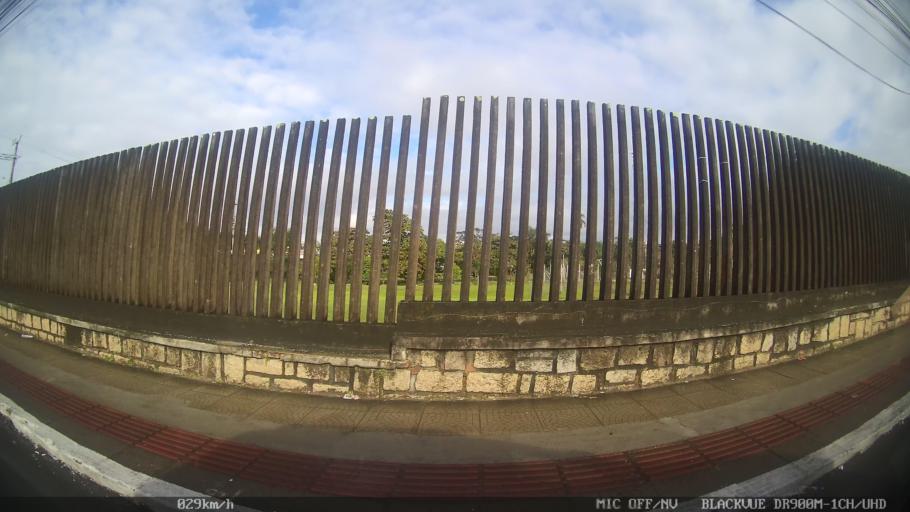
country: BR
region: Santa Catarina
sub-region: Sao Jose
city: Campinas
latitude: -27.6021
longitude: -48.6201
